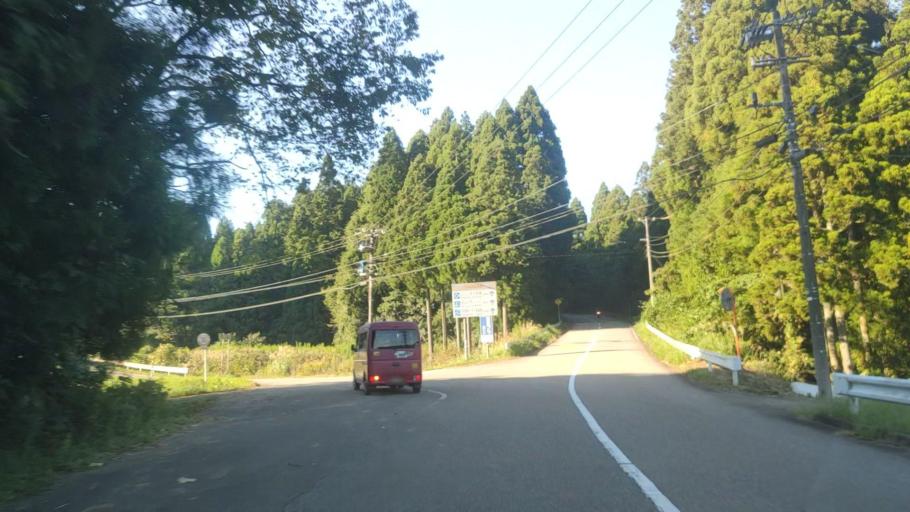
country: JP
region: Ishikawa
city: Nanao
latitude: 37.1092
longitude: 136.9618
